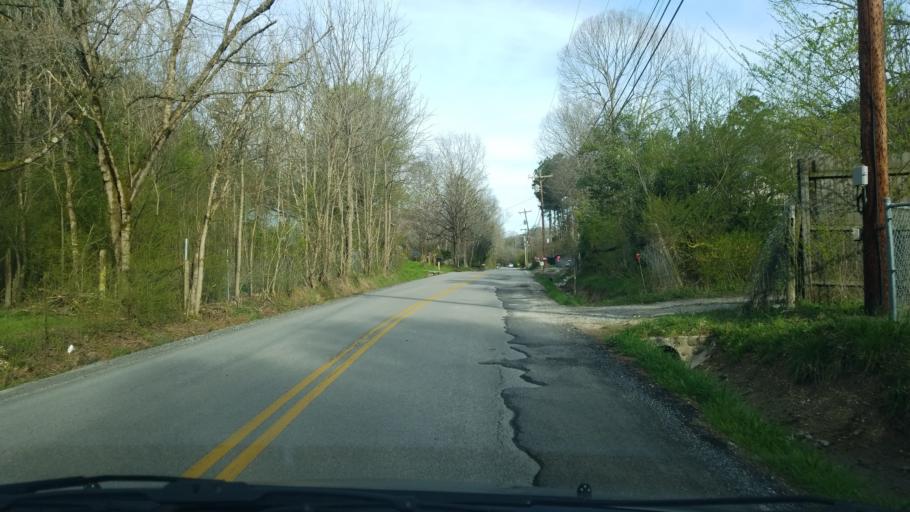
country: US
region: Tennessee
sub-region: Hamilton County
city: Collegedale
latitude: 35.0599
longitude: -85.1095
